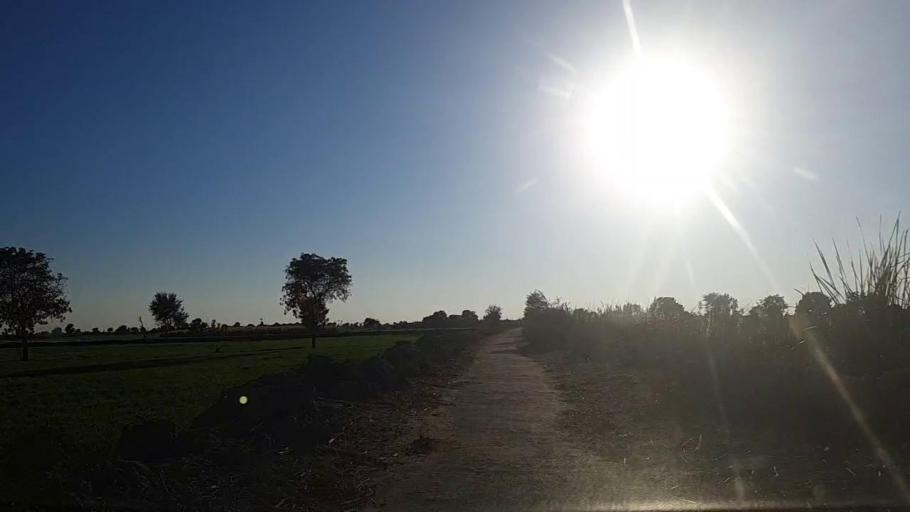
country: PK
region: Sindh
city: Sanghar
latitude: 26.1378
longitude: 68.9455
